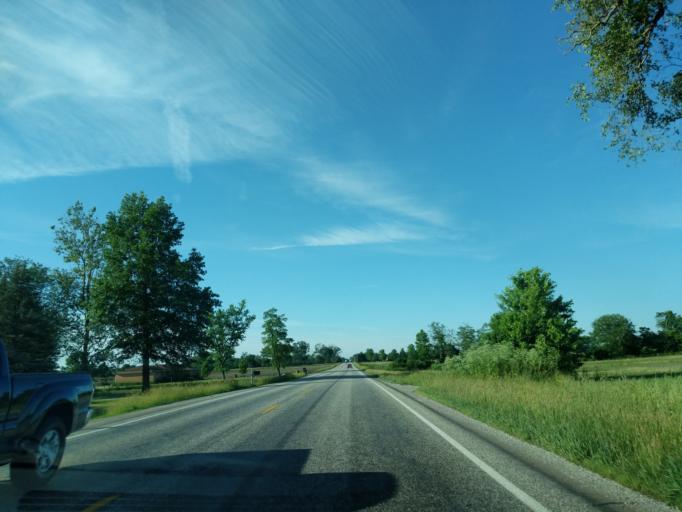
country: US
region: Indiana
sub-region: Madison County
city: Ingalls
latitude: 39.9242
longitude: -85.7711
